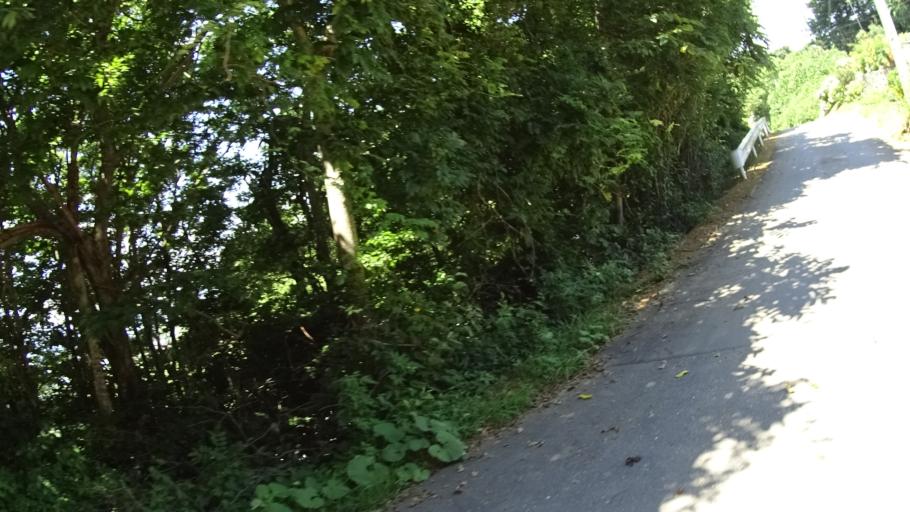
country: JP
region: Iwate
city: Ofunato
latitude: 38.8389
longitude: 141.6241
